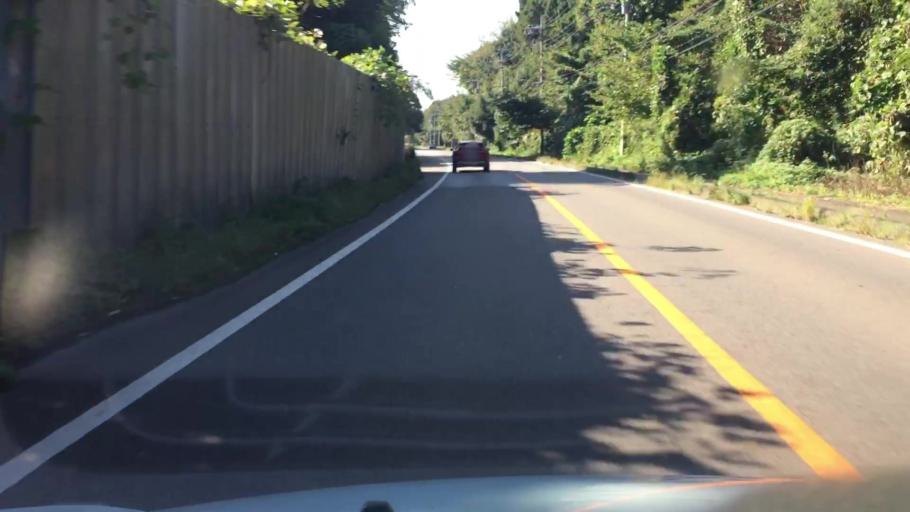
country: JP
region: Tochigi
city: Utsunomiya-shi
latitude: 36.5757
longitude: 139.9793
